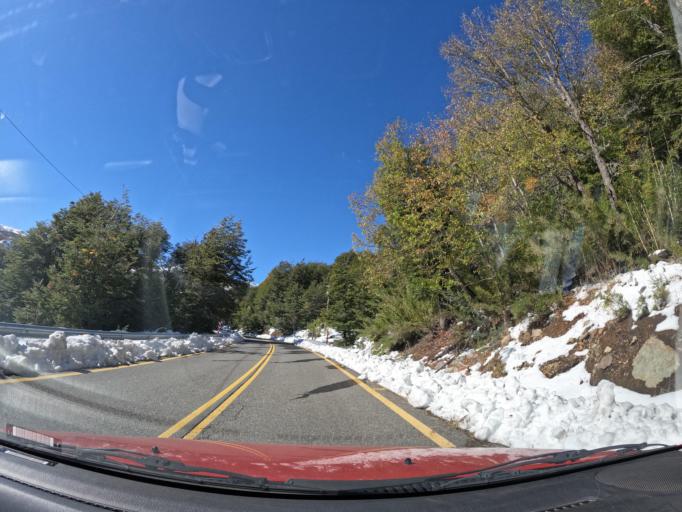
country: CL
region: Biobio
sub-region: Provincia de Nuble
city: Coihueco
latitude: -36.9180
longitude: -71.4316
